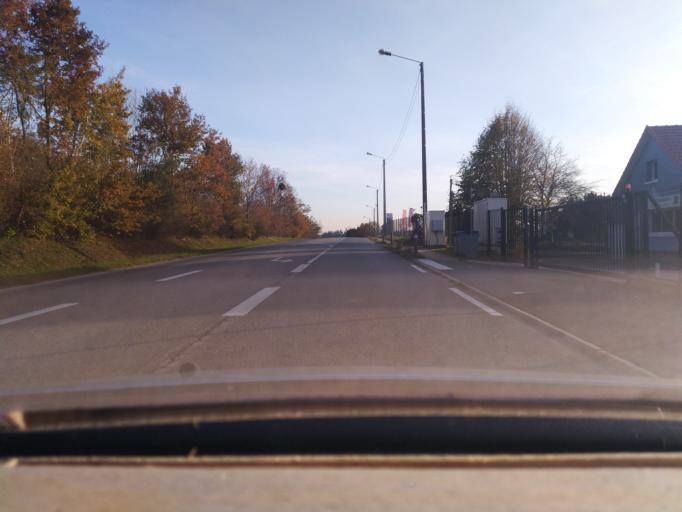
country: FR
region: Haute-Normandie
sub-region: Departement de la Seine-Maritime
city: Le Trait
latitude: 49.4645
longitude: 0.8199
